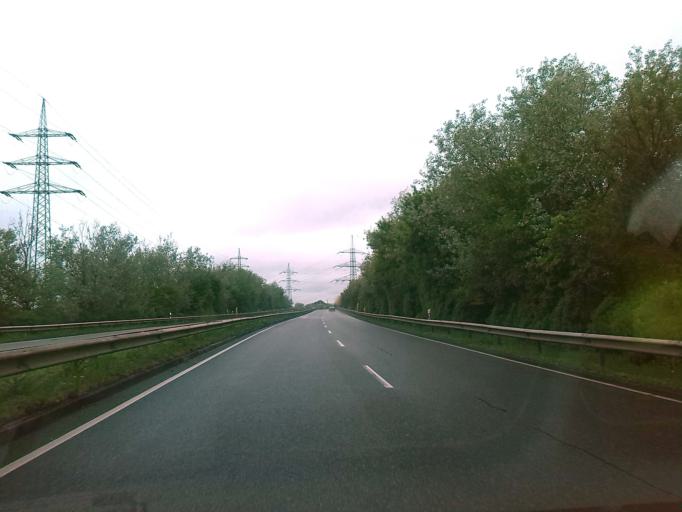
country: DE
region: Rheinland-Pfalz
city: Frankenthal
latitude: 49.5263
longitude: 8.4068
